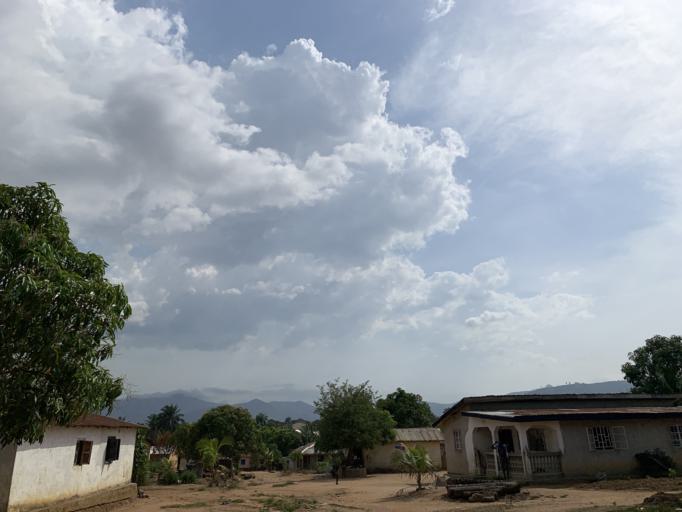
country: SL
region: Western Area
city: Waterloo
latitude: 8.3438
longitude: -13.0417
